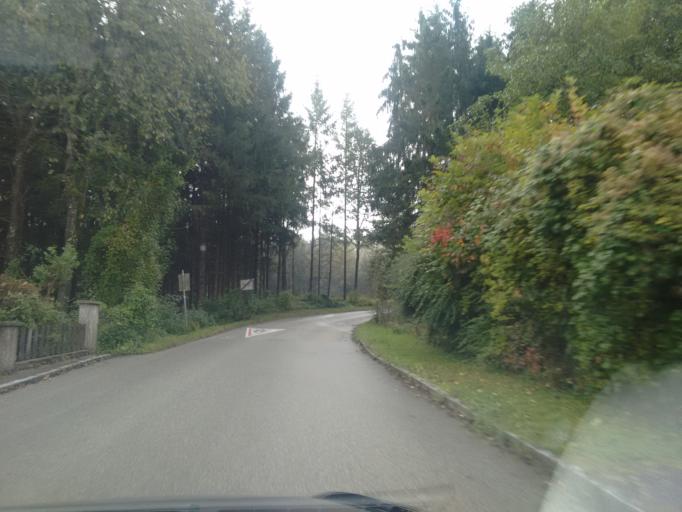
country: AT
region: Upper Austria
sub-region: Wels-Land
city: Gunskirchen
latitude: 48.1895
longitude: 13.9690
